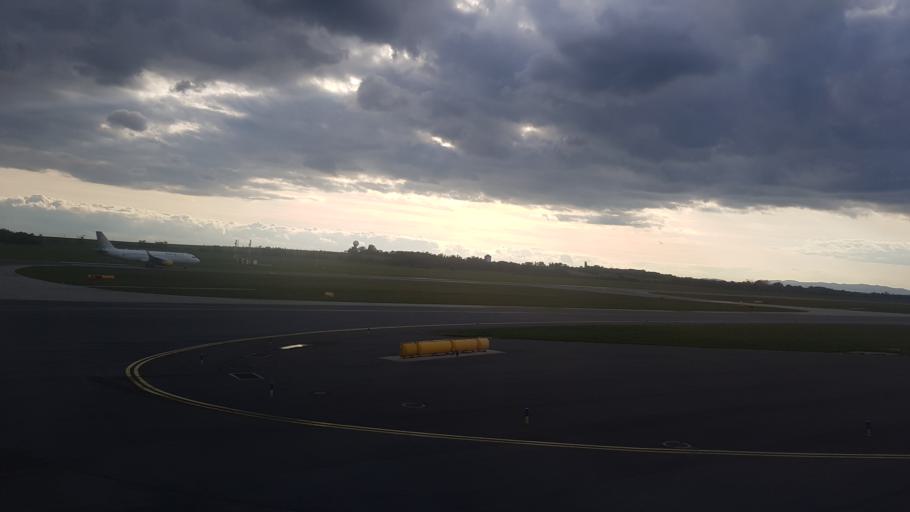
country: AT
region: Lower Austria
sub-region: Politischer Bezirk Bruck an der Leitha
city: Enzersdorf an der Fischa
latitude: 48.1119
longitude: 16.5760
